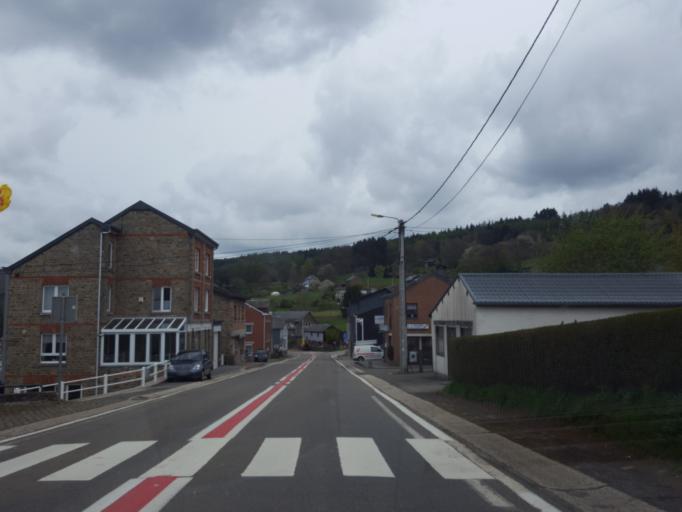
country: BE
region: Wallonia
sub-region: Province de Liege
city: Stoumont
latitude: 50.4081
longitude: 5.8081
